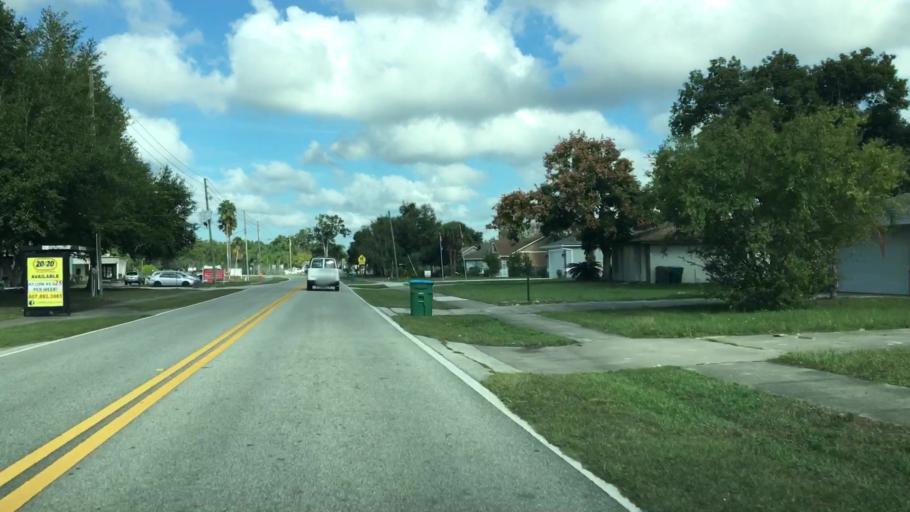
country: US
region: Florida
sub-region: Volusia County
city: Deltona
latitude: 28.8902
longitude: -81.2457
